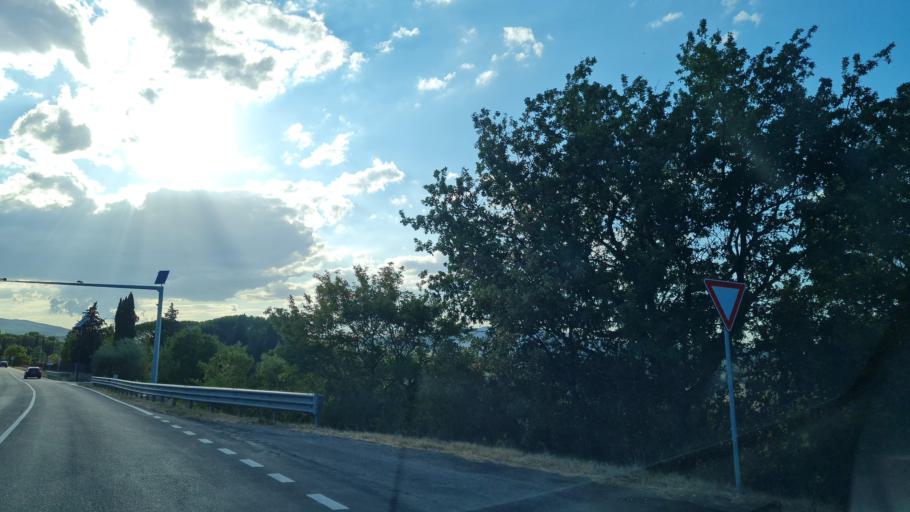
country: IT
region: Tuscany
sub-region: Provincia di Siena
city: Sarteano
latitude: 43.0281
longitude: 11.8766
